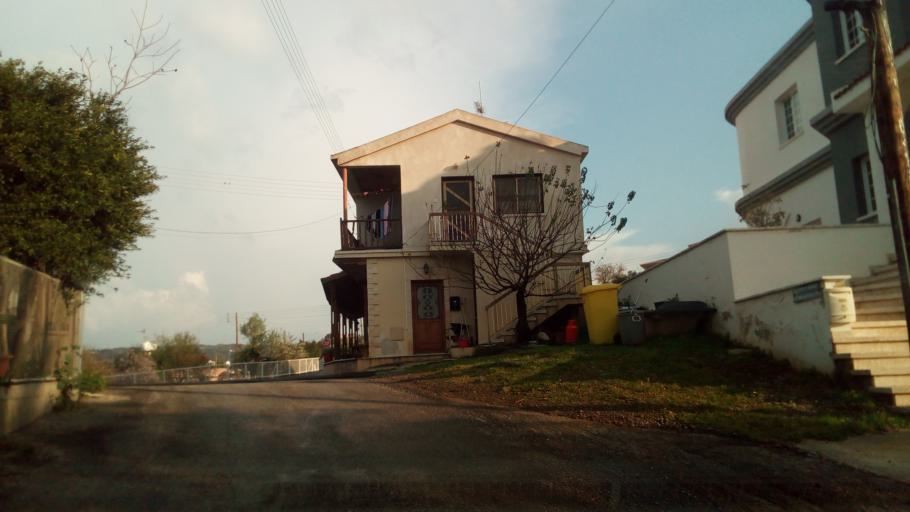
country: CY
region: Lefkosia
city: Kato Pyrgos
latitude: 35.1800
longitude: 32.6802
